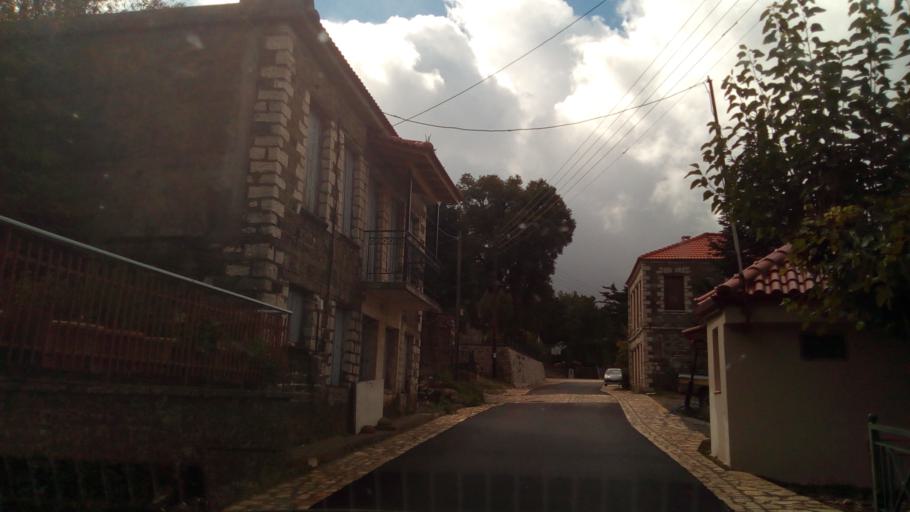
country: GR
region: West Greece
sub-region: Nomos Aitolias kai Akarnanias
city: Nafpaktos
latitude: 38.5339
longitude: 21.8187
